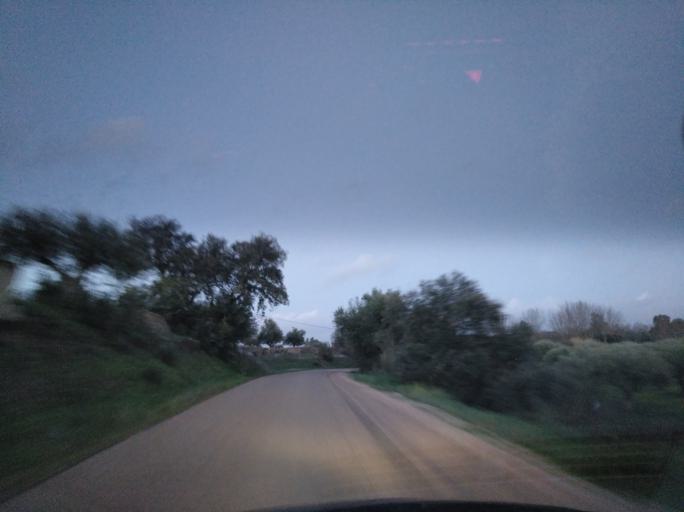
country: PT
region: Portalegre
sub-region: Campo Maior
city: Campo Maior
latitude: 39.0784
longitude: -7.0208
